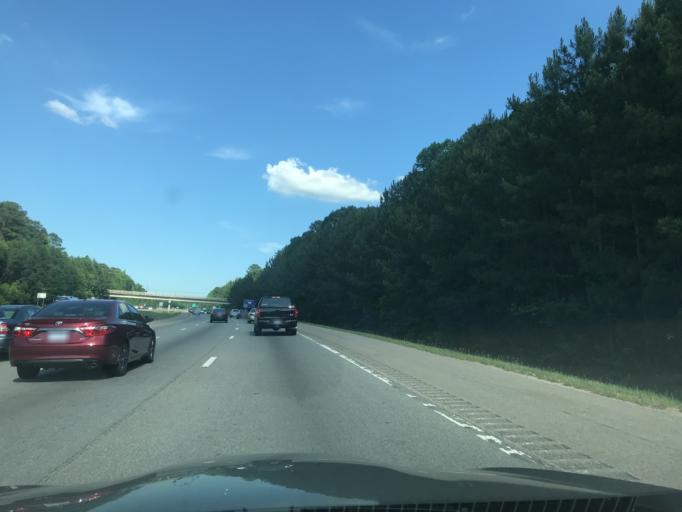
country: US
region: North Carolina
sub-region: Wake County
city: West Raleigh
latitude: 35.8997
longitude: -78.6263
